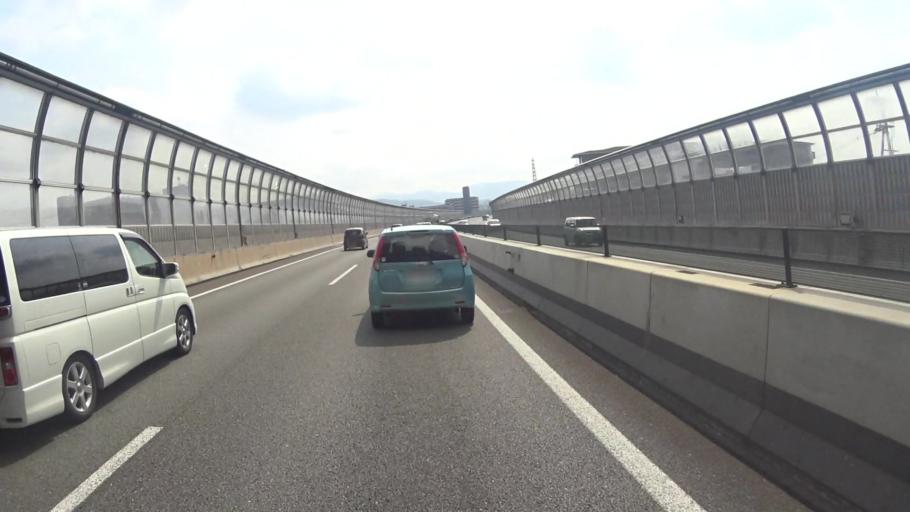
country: JP
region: Kyoto
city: Muko
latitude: 34.9563
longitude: 135.7520
